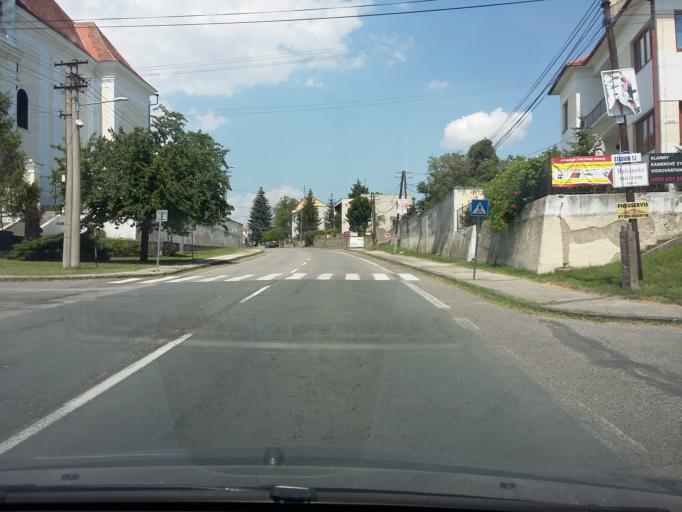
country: SK
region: Bratislavsky
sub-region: Okres Malacky
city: Malacky
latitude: 48.5005
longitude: 17.0029
